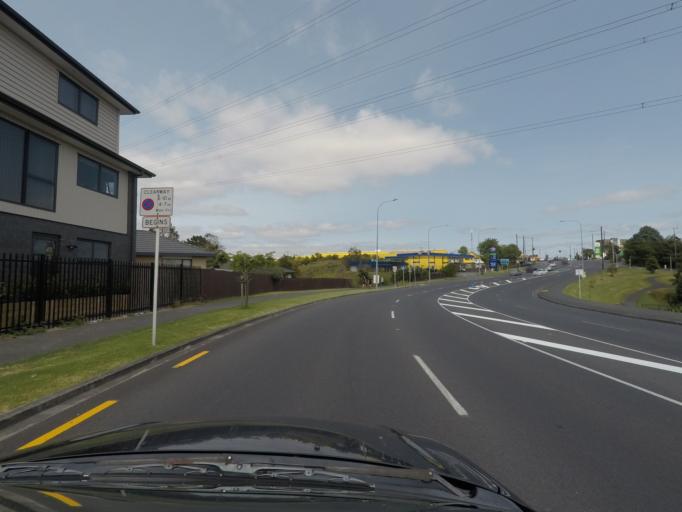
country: NZ
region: Auckland
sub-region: Auckland
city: Waitakere
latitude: -36.9106
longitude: 174.6920
